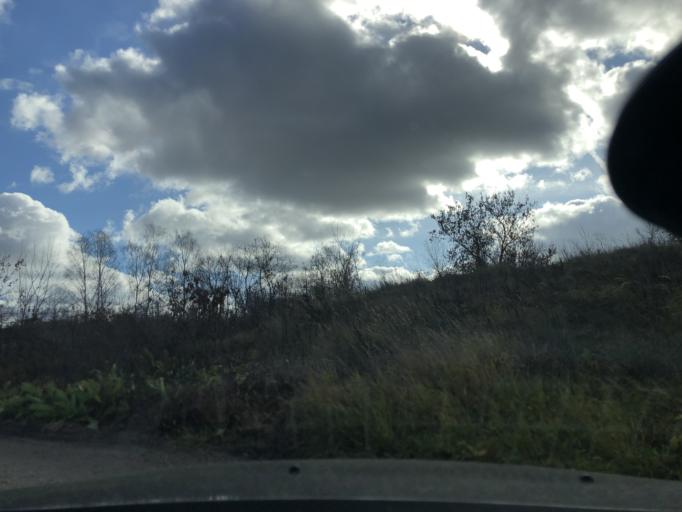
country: RU
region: Tula
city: Gorelki
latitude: 54.2959
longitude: 37.5614
